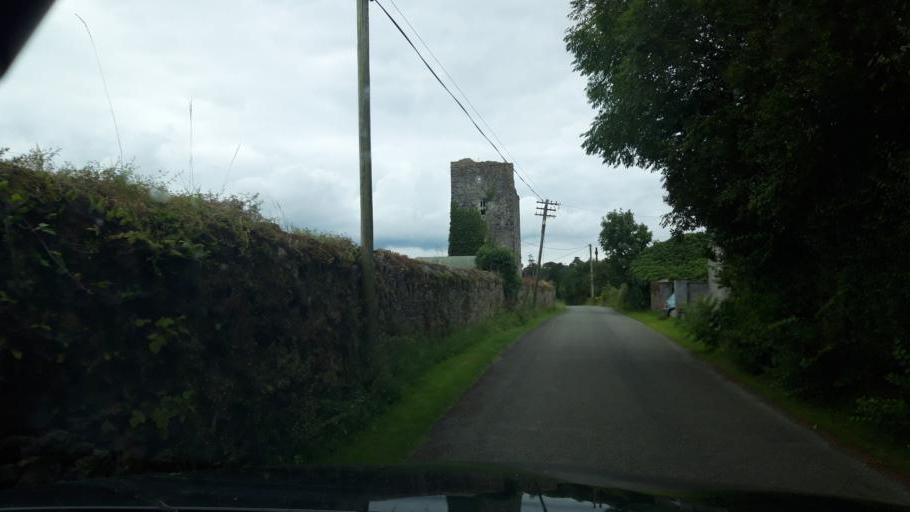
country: IE
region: Leinster
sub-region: Kilkenny
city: Thomastown
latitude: 52.6255
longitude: -7.0675
